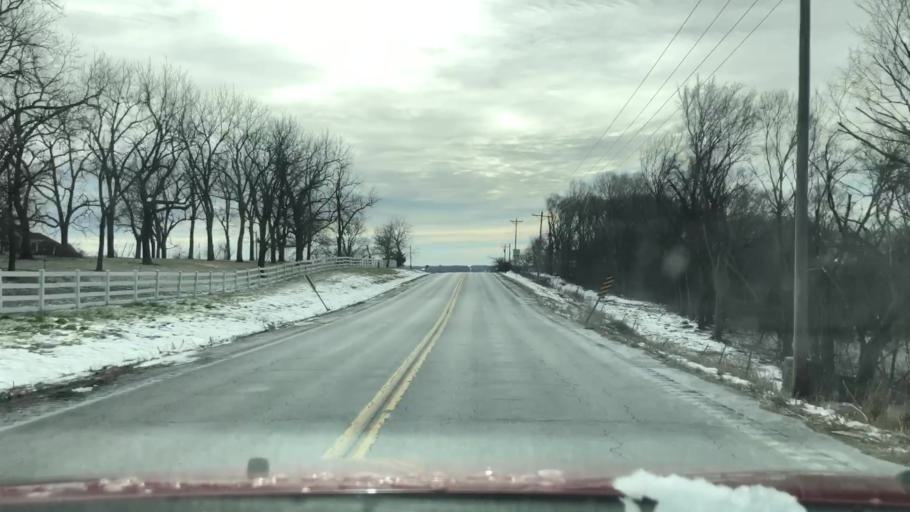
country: US
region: Missouri
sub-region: Jackson County
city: Oak Grove
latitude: 38.9320
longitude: -94.1325
